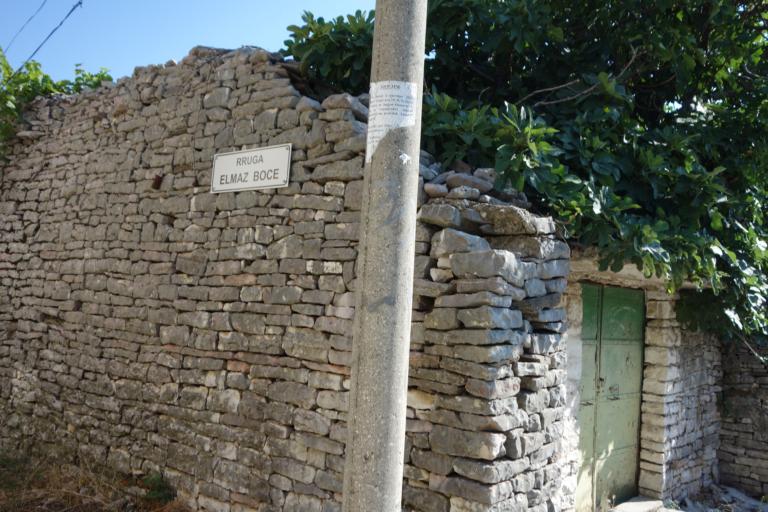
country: AL
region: Gjirokaster
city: Gjirokaster
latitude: 40.0674
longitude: 20.1359
